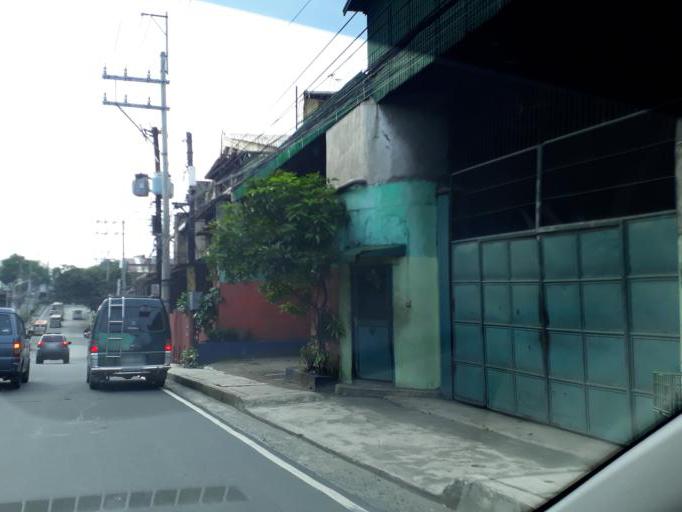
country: PH
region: Metro Manila
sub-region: Caloocan City
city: Niugan
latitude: 14.6665
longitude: 120.9799
